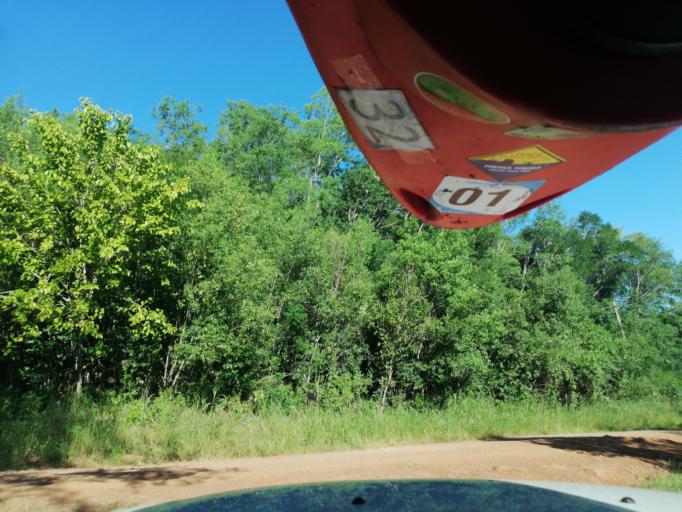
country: AR
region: Misiones
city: Martires
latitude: -27.4216
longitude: -55.4216
